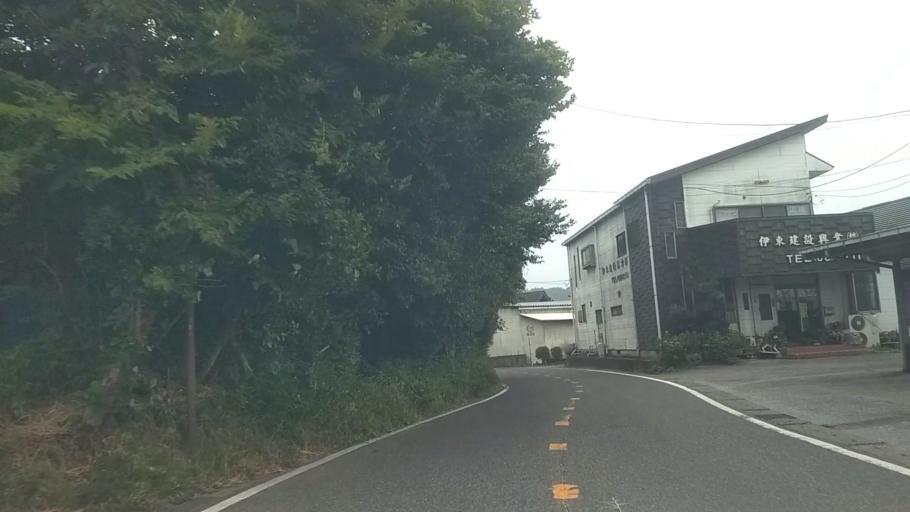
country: JP
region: Chiba
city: Kimitsu
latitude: 35.2160
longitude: 139.9214
